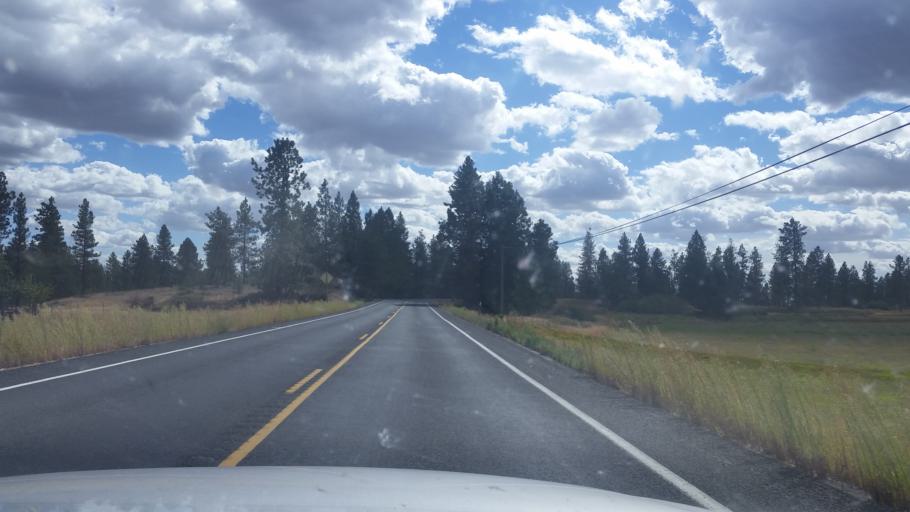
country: US
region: Washington
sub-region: Spokane County
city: Medical Lake
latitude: 47.5457
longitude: -117.7046
